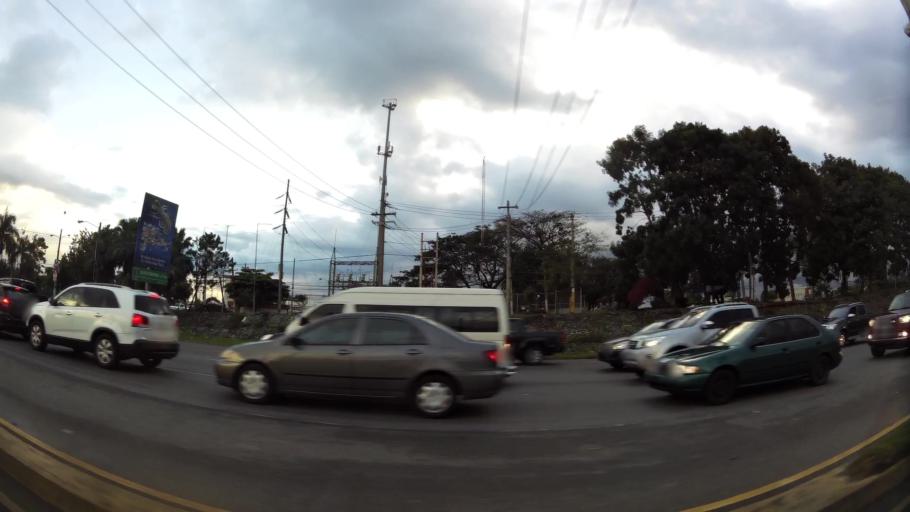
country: DO
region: Santo Domingo
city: Santo Domingo Oeste
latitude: 18.5577
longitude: -70.0582
